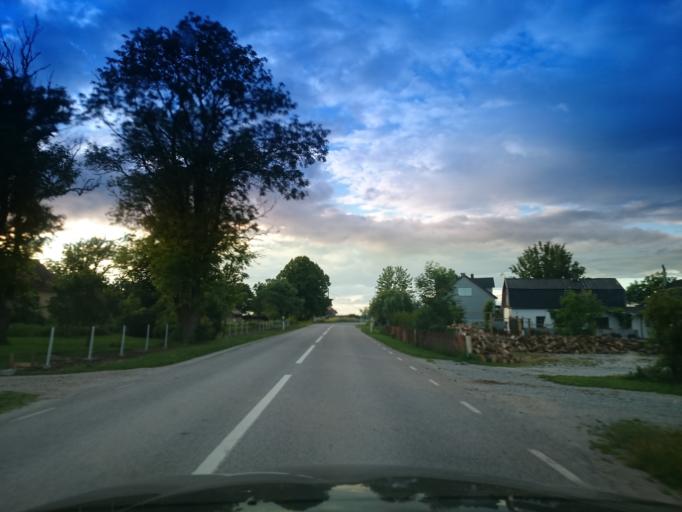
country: SE
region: Gotland
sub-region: Gotland
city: Vibble
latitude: 57.5031
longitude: 18.3715
